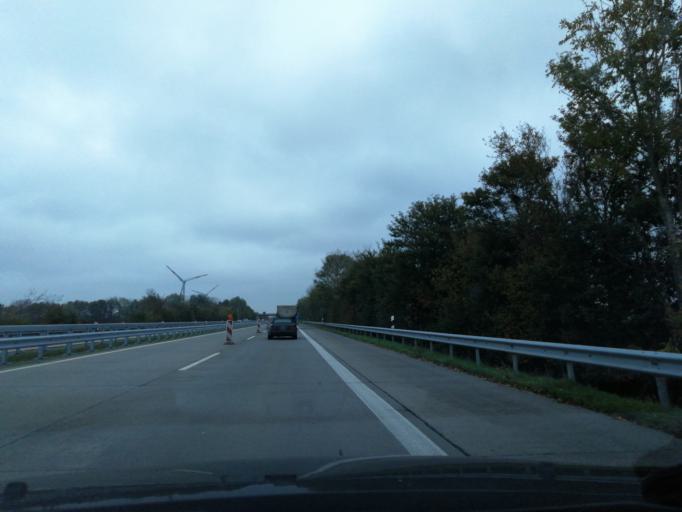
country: DE
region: Lower Saxony
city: Fedderwarden
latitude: 53.5382
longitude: 8.0294
